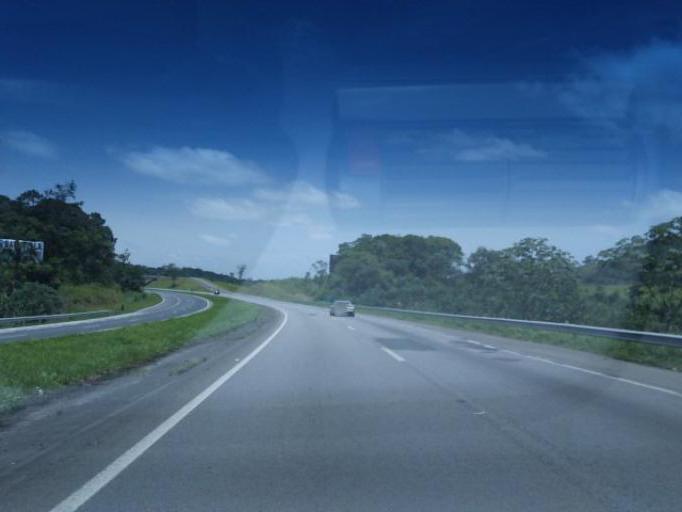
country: BR
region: Sao Paulo
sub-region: Miracatu
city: Miracatu
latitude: -24.2930
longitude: -47.4762
